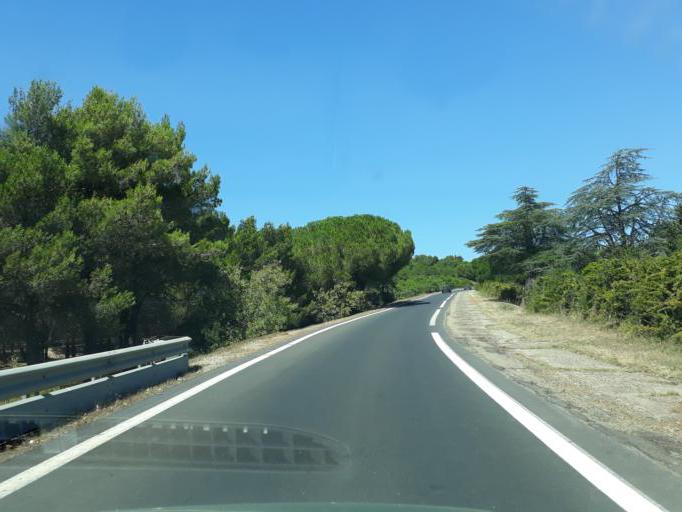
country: FR
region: Languedoc-Roussillon
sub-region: Departement de l'Herault
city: Le Cap d'Agde
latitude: 43.2930
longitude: 3.5056
